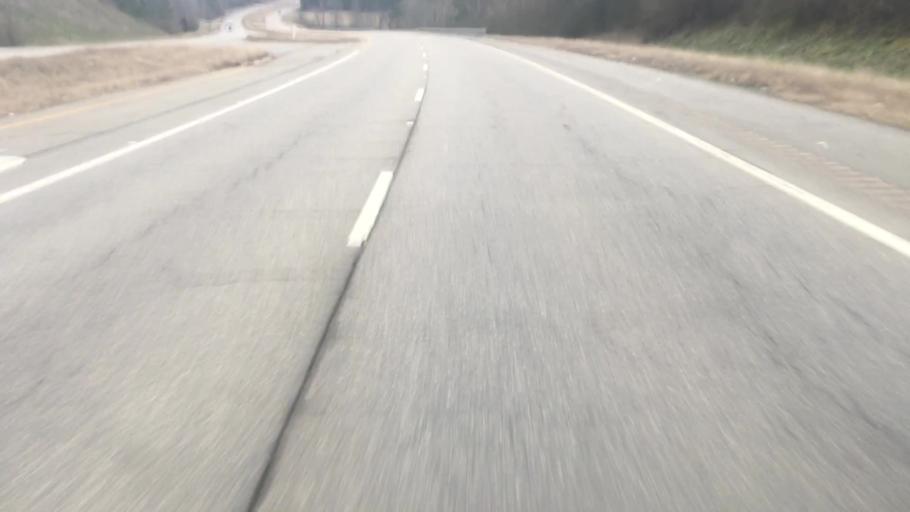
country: US
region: Alabama
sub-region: Walker County
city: Dora
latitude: 33.7947
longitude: -87.1065
